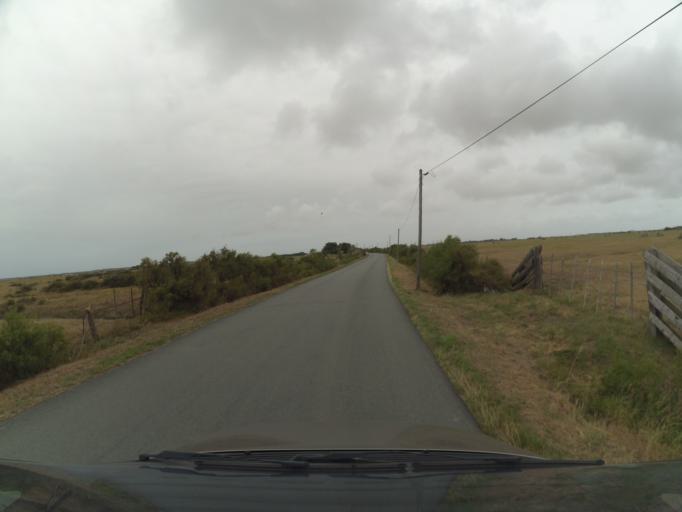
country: FR
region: Pays de la Loire
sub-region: Departement de la Vendee
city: La Barre-de-Monts
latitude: 46.8819
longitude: -2.0832
